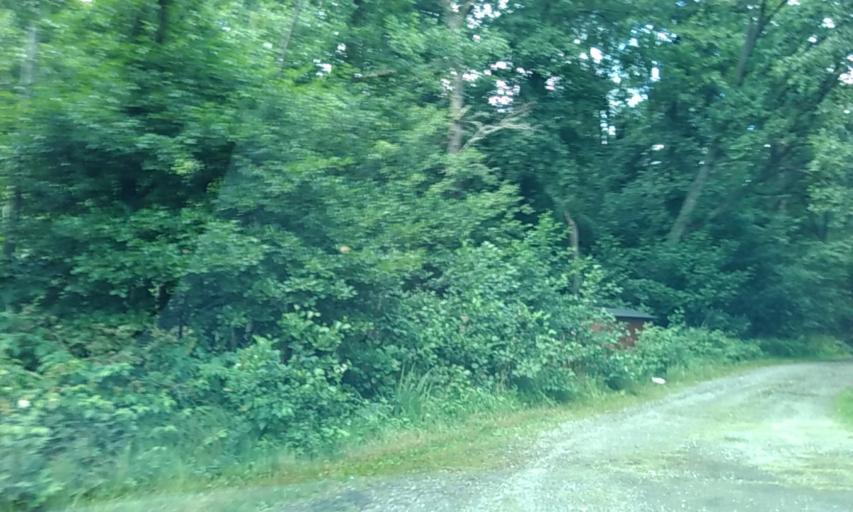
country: SE
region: Vaestra Goetaland
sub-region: Lerums Kommun
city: Grabo
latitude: 57.9073
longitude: 12.3759
